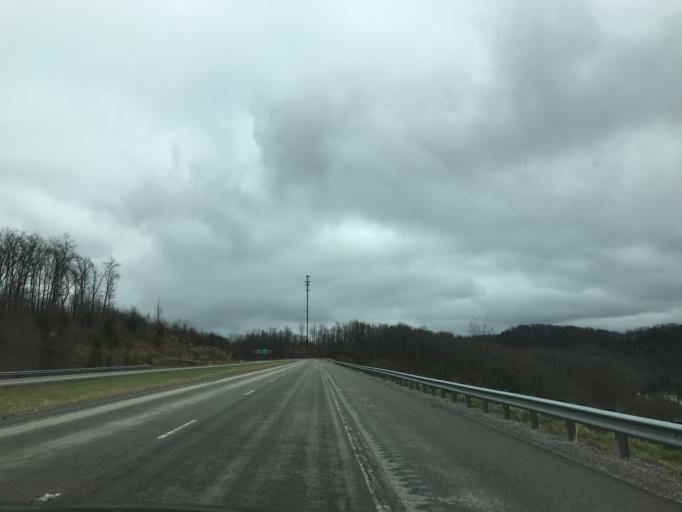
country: US
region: West Virginia
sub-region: Raleigh County
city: Sophia
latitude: 37.7146
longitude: -81.2700
